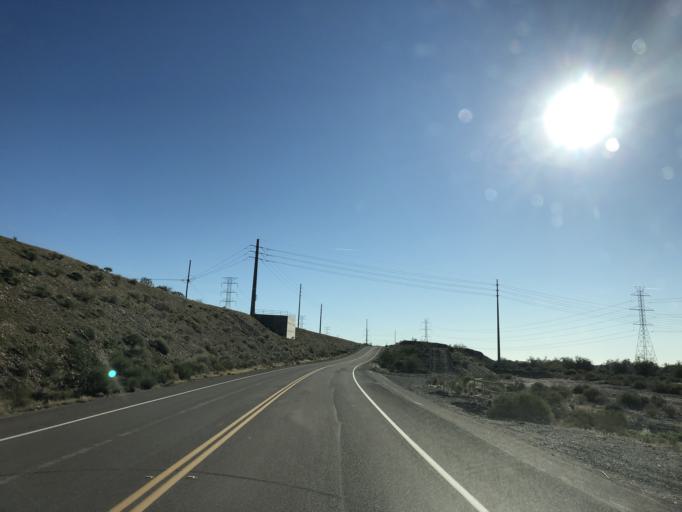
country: US
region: Arizona
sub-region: Maricopa County
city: Sun City West
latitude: 33.6828
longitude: -112.2977
